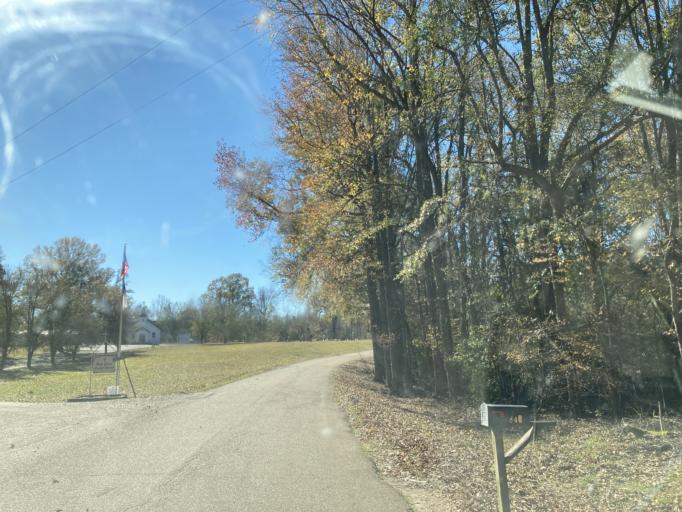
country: US
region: Mississippi
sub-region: Hinds County
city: Lynchburg
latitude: 32.5543
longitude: -90.5915
